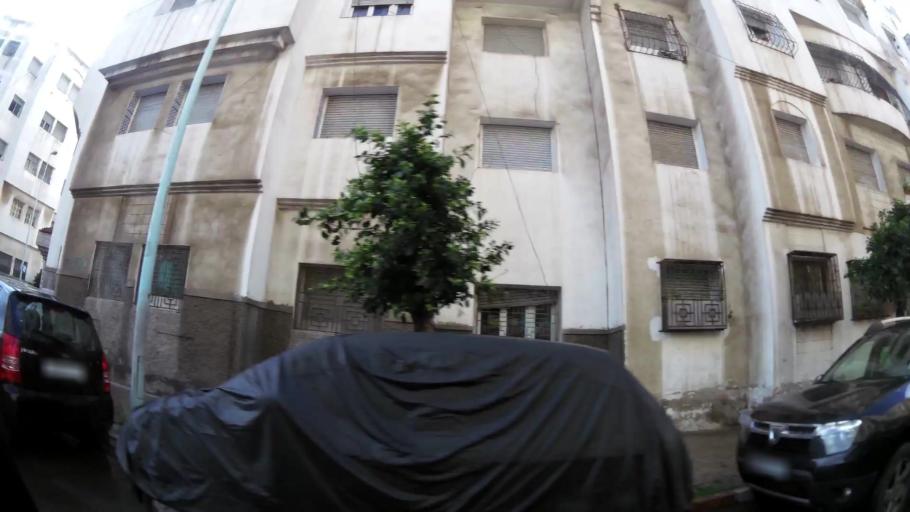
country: MA
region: Grand Casablanca
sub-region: Mediouna
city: Tit Mellil
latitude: 33.5987
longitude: -7.5241
